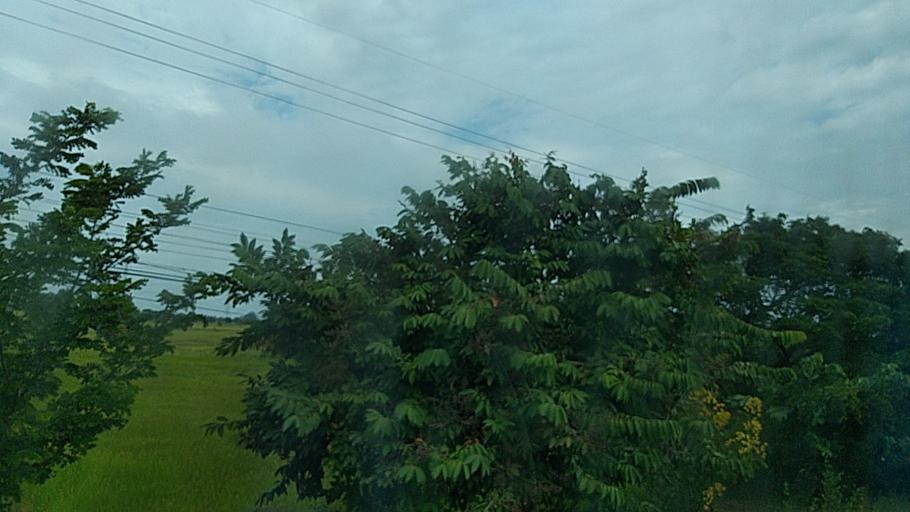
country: TH
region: Roi Et
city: Changhan
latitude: 16.1220
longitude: 103.4824
